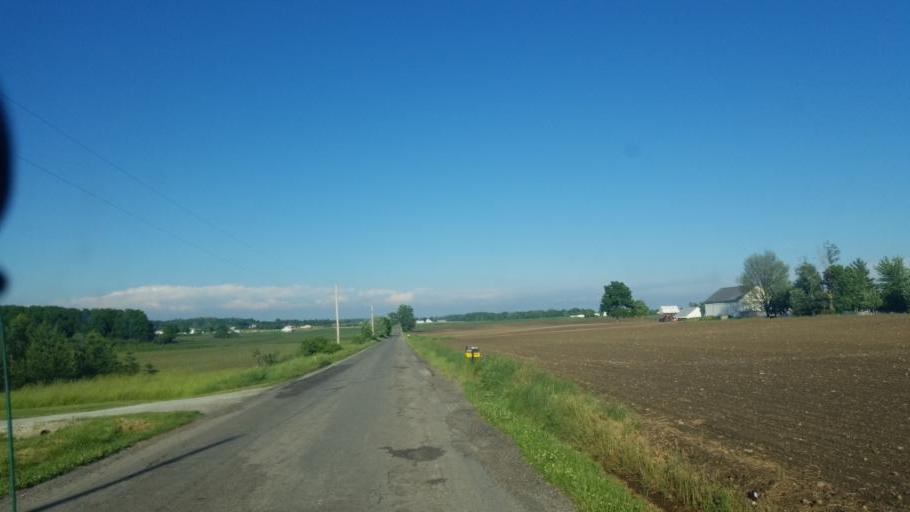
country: US
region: Indiana
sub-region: Marshall County
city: Bremen
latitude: 41.4265
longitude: -86.0942
